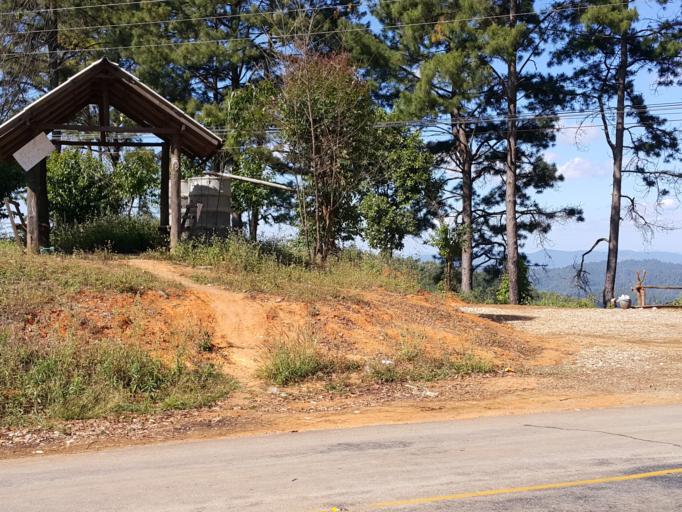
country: TH
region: Chiang Mai
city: Wiang Haeng
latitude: 19.5178
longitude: 98.7569
